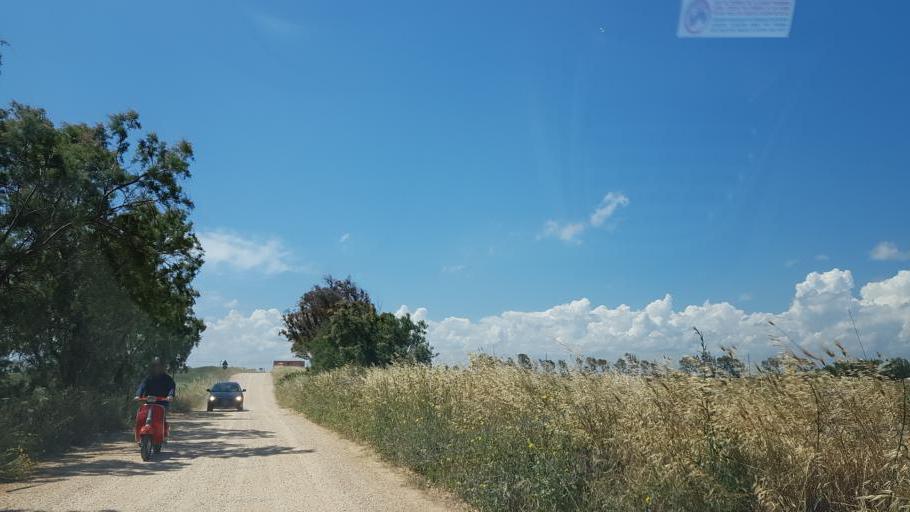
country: IT
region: Apulia
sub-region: Provincia di Brindisi
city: San Vito dei Normanni
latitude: 40.6963
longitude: 17.8198
